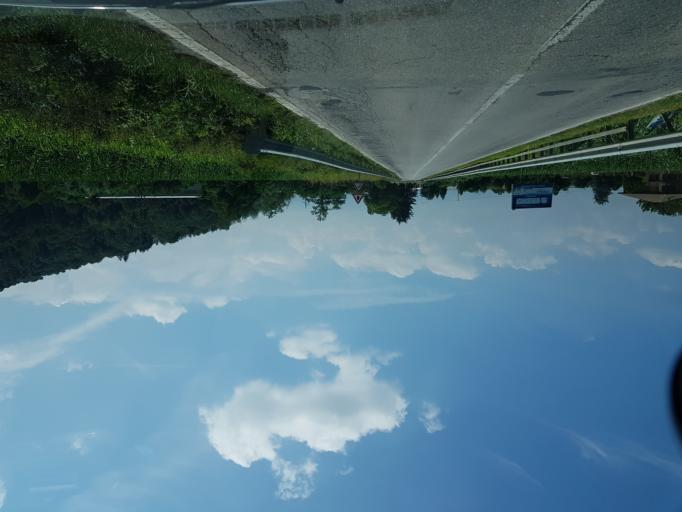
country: IT
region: Piedmont
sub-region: Provincia di Cuneo
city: Caraglio
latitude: 44.4344
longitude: 7.4201
